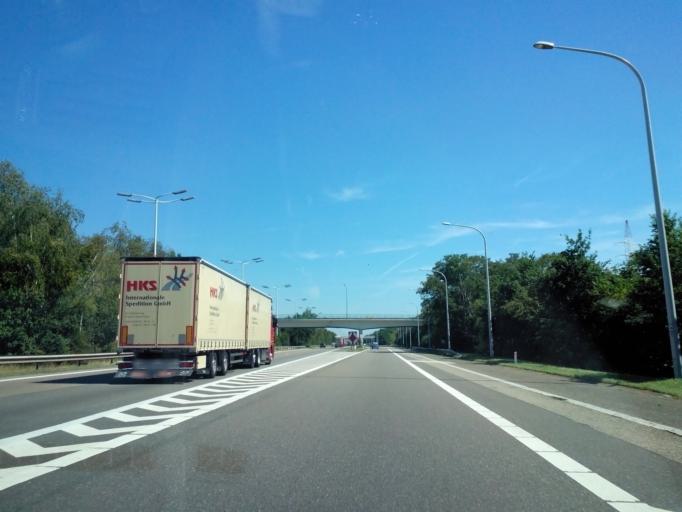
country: BE
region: Flanders
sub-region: Provincie Limburg
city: Genk
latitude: 50.9947
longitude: 5.4932
